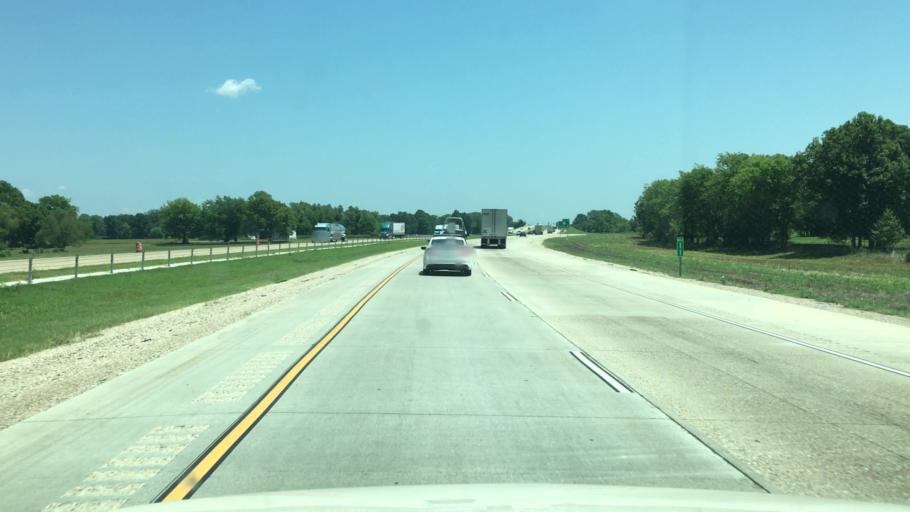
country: US
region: Arkansas
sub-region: Miller County
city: Texarkana
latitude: 33.5478
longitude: -93.8833
